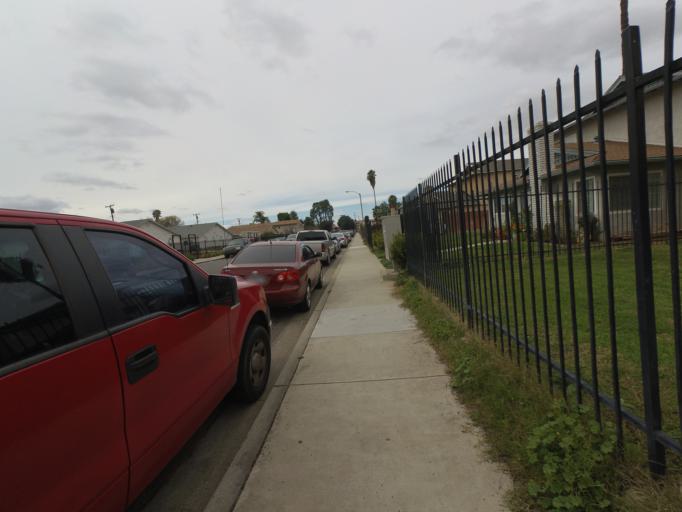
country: US
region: California
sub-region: Riverside County
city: March Air Force Base
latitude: 33.9191
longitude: -117.2629
